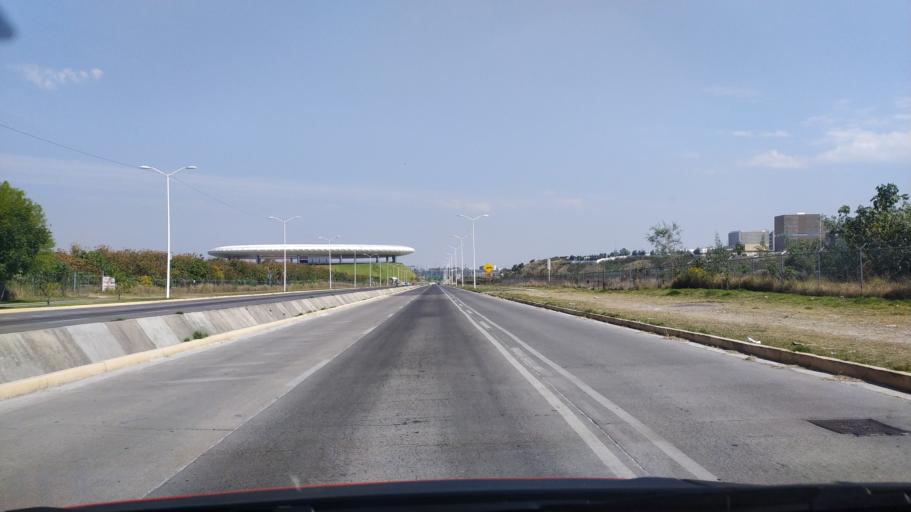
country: MX
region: Jalisco
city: Guadalajara
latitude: 20.6791
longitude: -103.4629
